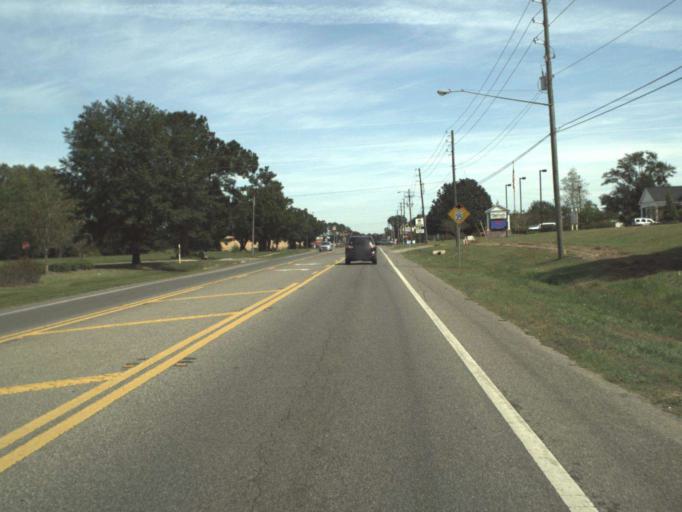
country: US
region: Florida
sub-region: Washington County
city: Chipley
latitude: 30.7608
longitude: -85.5455
